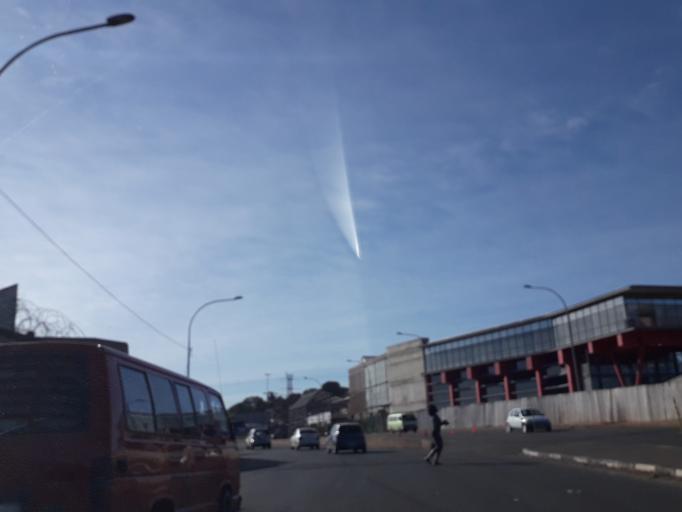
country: ZA
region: Gauteng
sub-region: City of Johannesburg Metropolitan Municipality
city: Johannesburg
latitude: -26.1848
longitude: 27.9821
